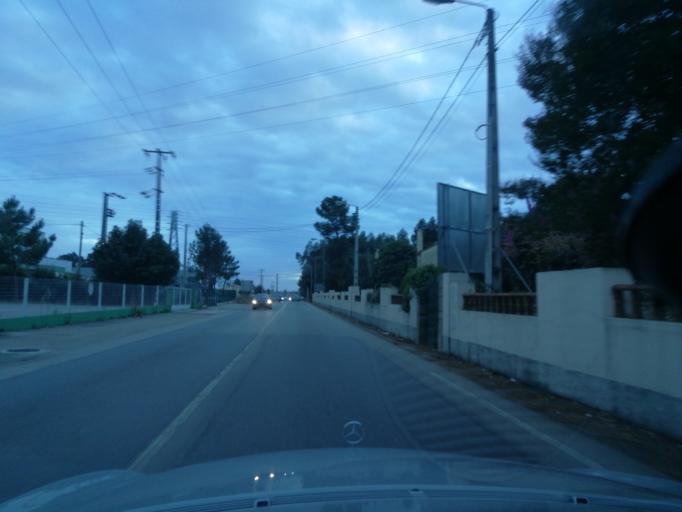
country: PT
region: Aveiro
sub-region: Estarreja
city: Beduido
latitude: 40.7748
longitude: -8.5684
